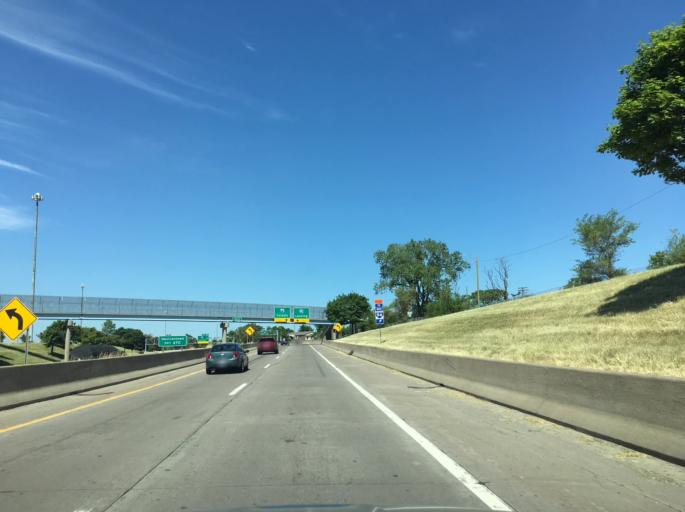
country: US
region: Michigan
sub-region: Wayne County
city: Detroit
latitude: 42.3329
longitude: -83.0793
